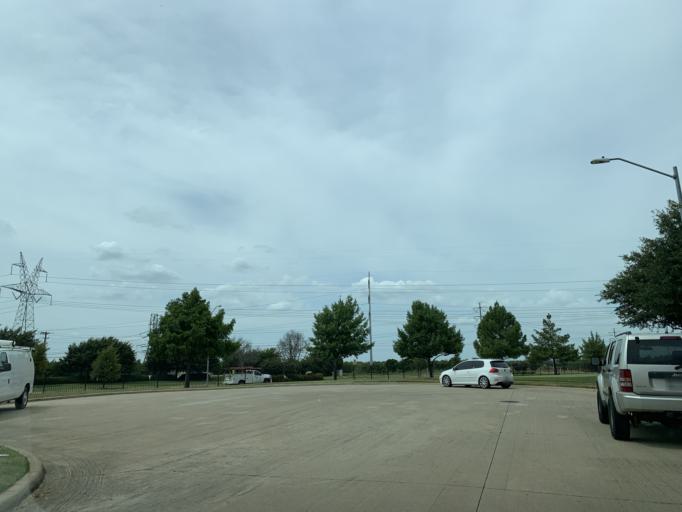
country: US
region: Texas
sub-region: Dallas County
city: Grand Prairie
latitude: 32.6527
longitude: -97.0418
